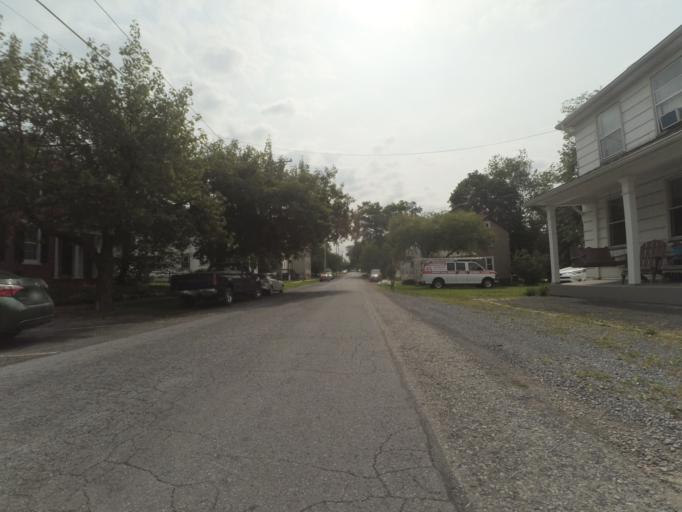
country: US
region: Pennsylvania
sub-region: Huntingdon County
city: McConnellstown
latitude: 40.5584
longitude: -78.0984
